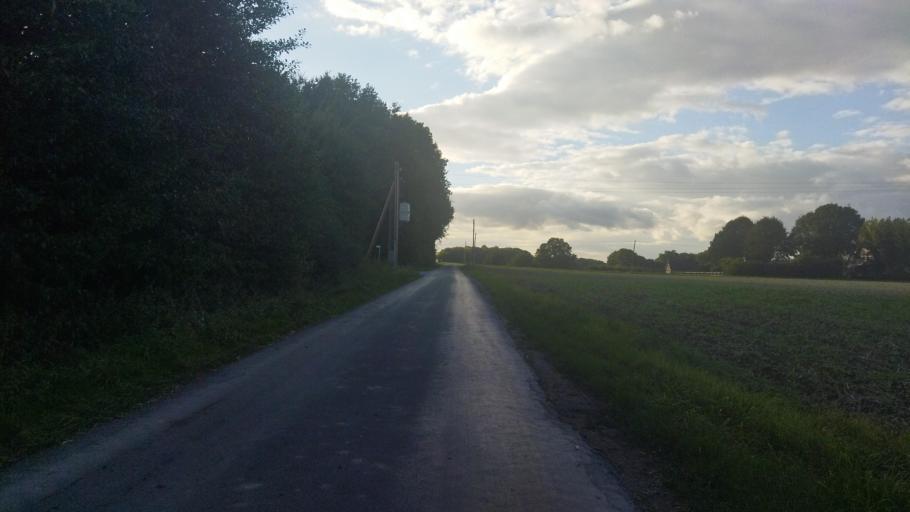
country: DE
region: North Rhine-Westphalia
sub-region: Regierungsbezirk Munster
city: Billerbeck
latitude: 51.9573
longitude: 7.2643
